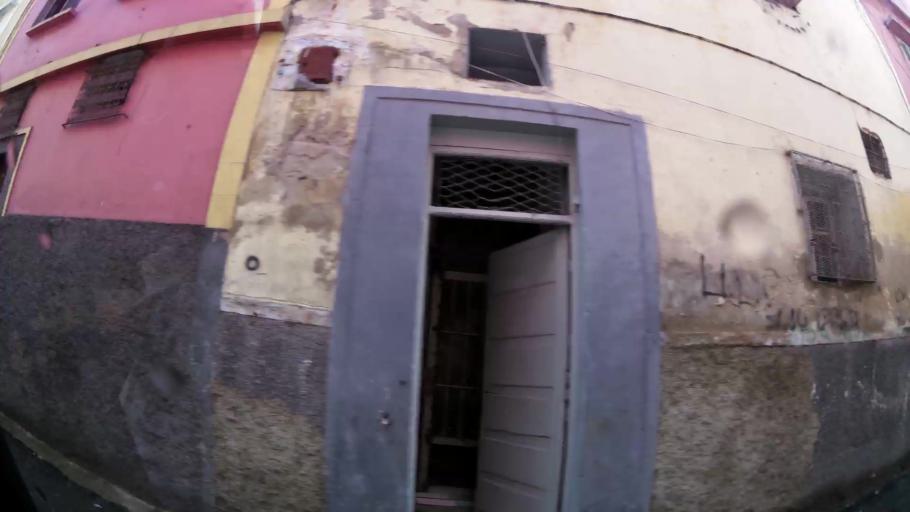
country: MA
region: Grand Casablanca
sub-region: Casablanca
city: Casablanca
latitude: 33.5766
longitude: -7.5919
